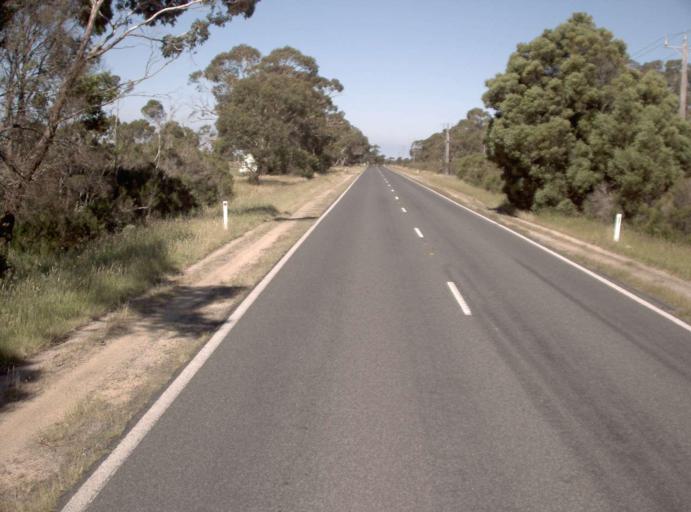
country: AU
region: Victoria
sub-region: Latrobe
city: Morwell
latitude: -38.6326
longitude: 146.5533
